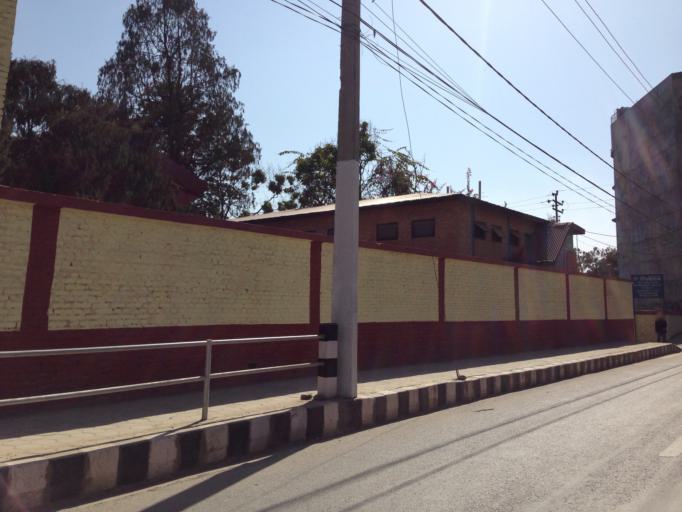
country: NP
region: Central Region
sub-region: Bagmati Zone
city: Kathmandu
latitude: 27.7362
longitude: 85.3327
